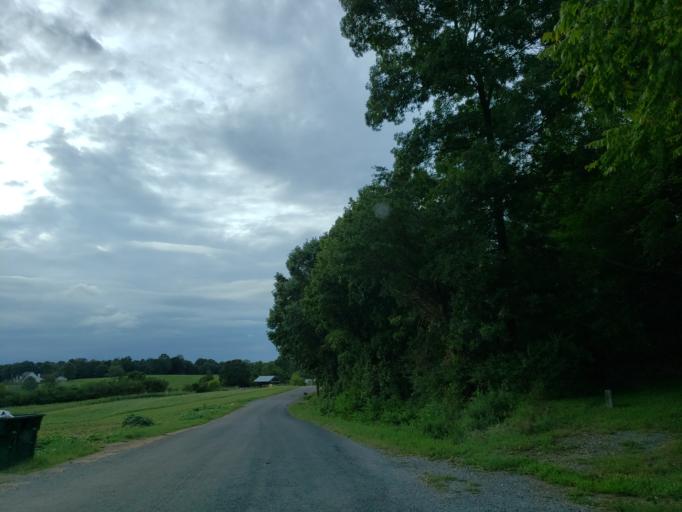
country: US
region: Georgia
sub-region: Pickens County
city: Jasper
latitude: 34.4727
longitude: -84.5106
